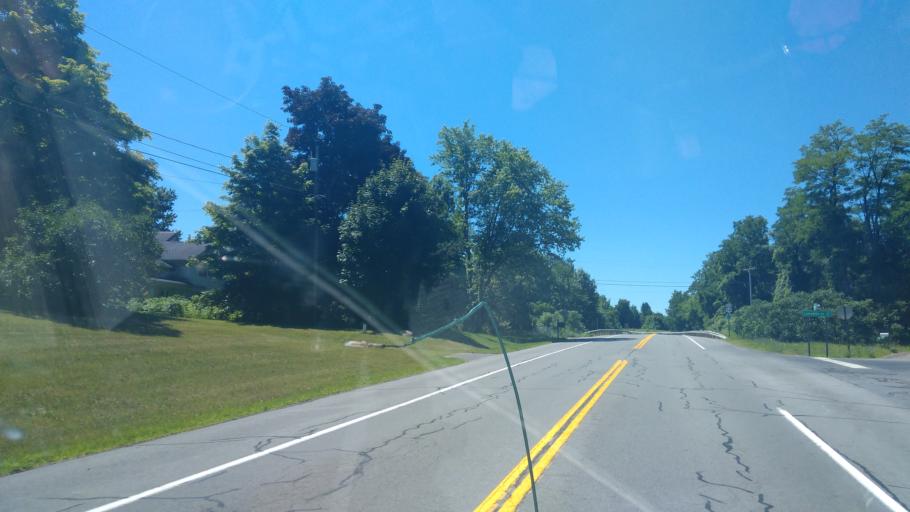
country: US
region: New York
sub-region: Wayne County
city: Lyons
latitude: 43.1643
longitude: -76.9877
